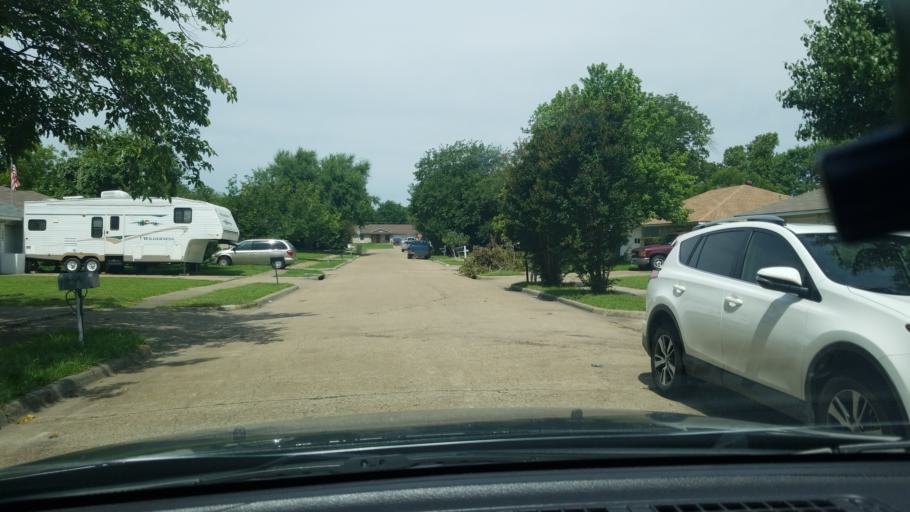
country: US
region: Texas
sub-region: Dallas County
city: Mesquite
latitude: 32.7549
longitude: -96.5773
